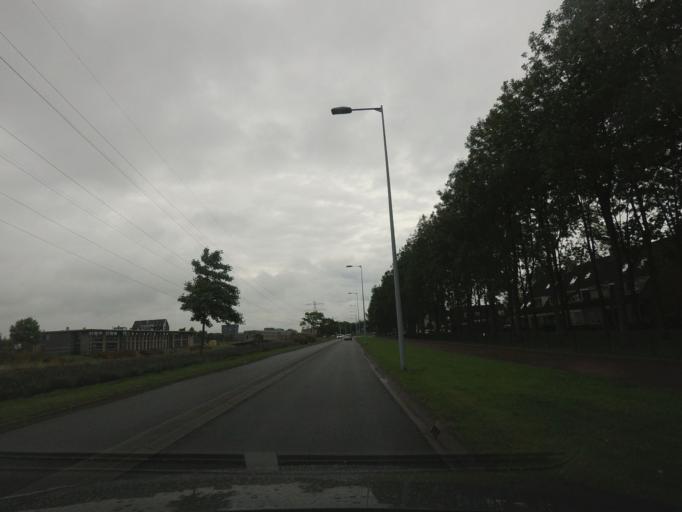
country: NL
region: North Holland
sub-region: Gemeente Haarlemmermeer
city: Hoofddorp
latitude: 52.3168
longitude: 4.6504
